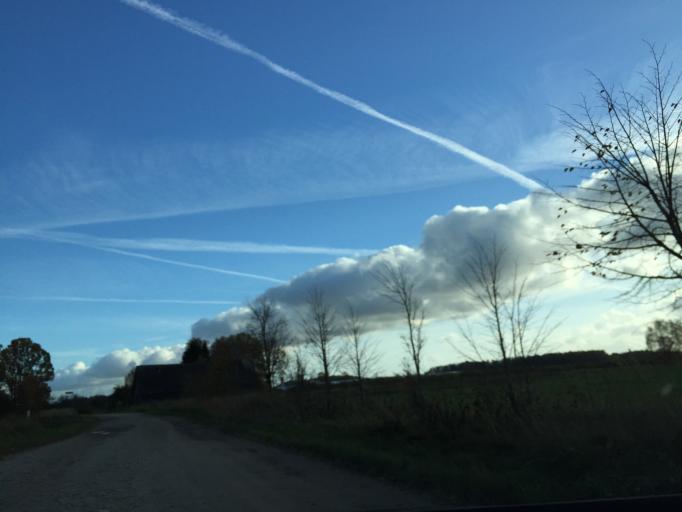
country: LV
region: Ogre
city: Jumprava
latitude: 56.7651
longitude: 24.9776
